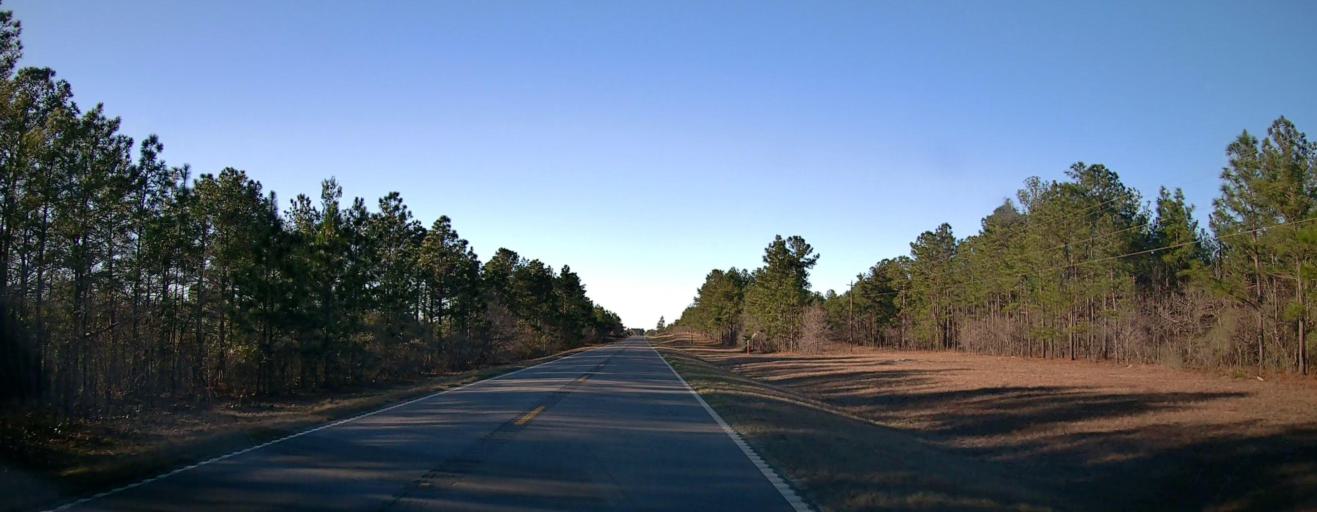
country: US
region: Georgia
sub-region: Talbot County
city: Talbotton
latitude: 32.5774
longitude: -84.4443
